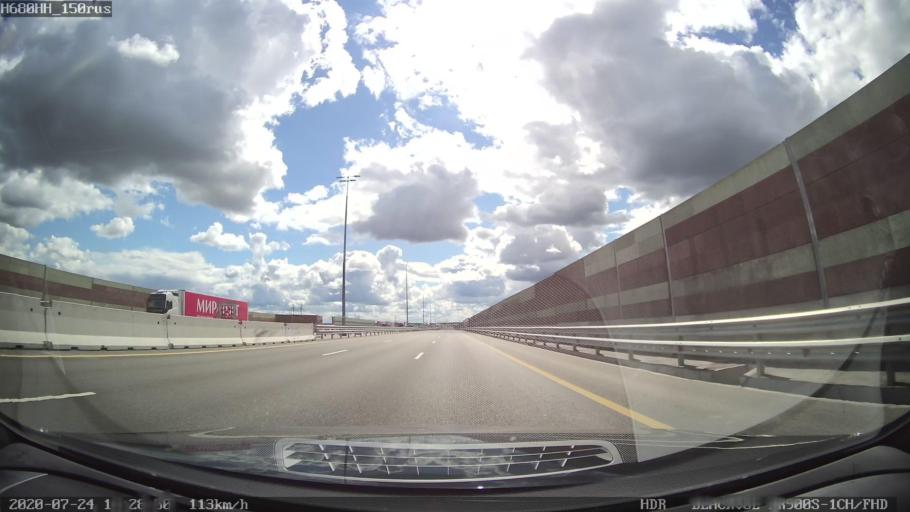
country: RU
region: Leningrad
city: Fedorovskoye
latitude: 59.6905
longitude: 30.5743
